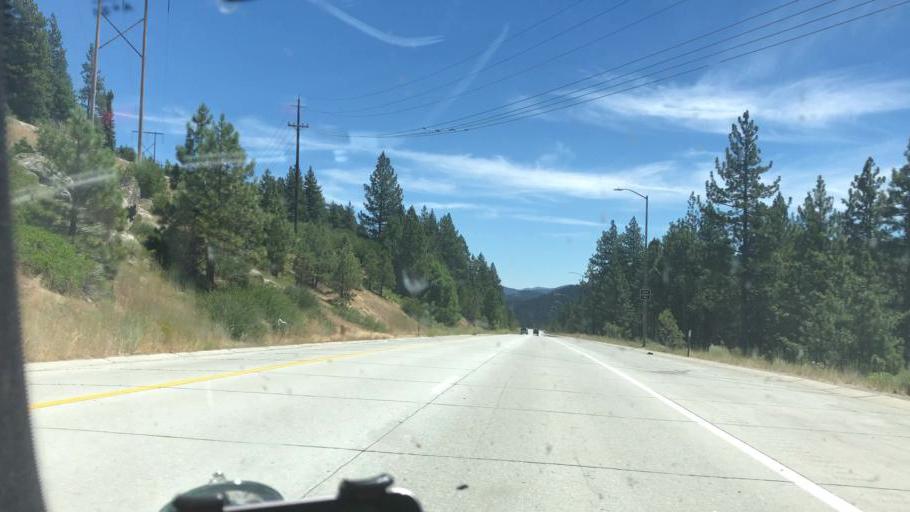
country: US
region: California
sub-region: Nevada County
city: Truckee
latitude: 39.3299
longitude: -120.2844
